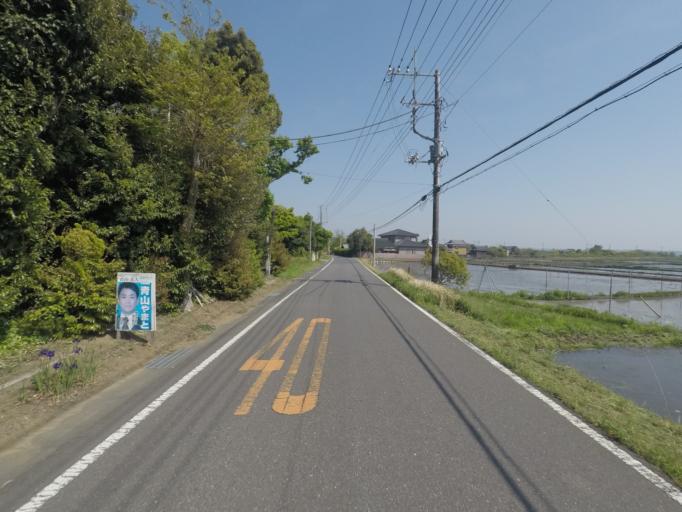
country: JP
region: Ibaraki
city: Ami
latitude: 36.0719
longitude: 140.2755
